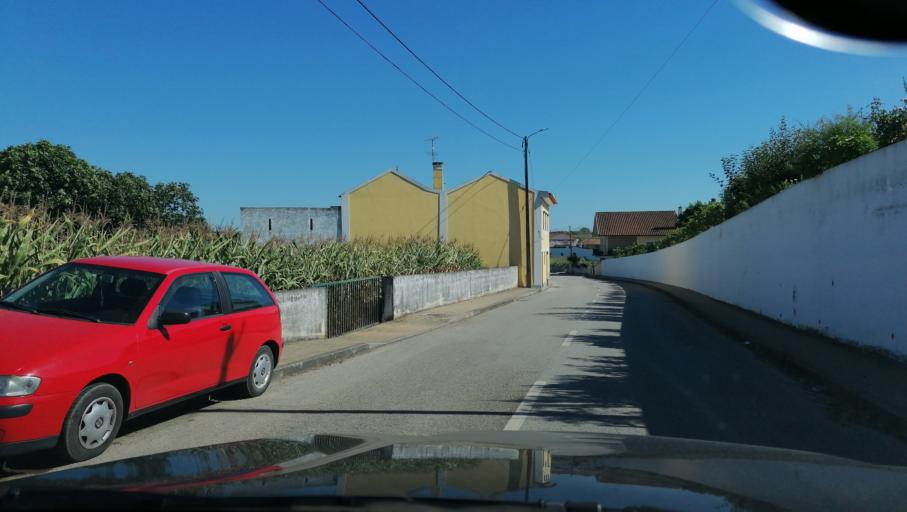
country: PT
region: Aveiro
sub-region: Estarreja
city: Salreu
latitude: 40.7478
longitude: -8.5482
